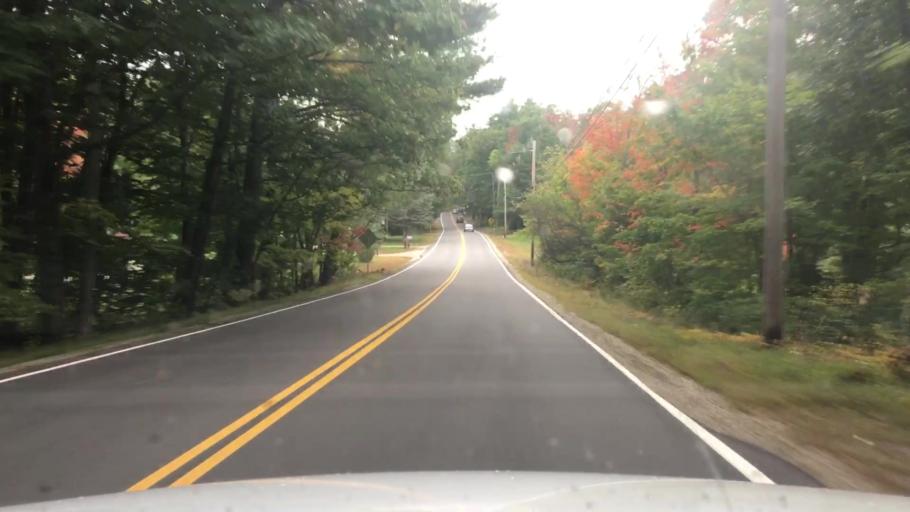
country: US
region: New Hampshire
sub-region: Belknap County
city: Gilford
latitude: 43.5474
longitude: -71.3064
